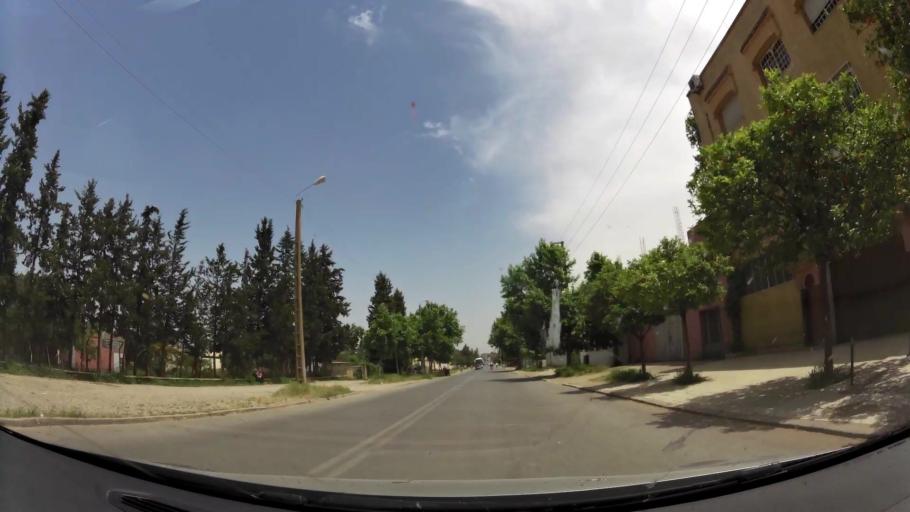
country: MA
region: Rabat-Sale-Zemmour-Zaer
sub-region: Khemisset
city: Khemisset
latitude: 33.8210
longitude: -6.0811
